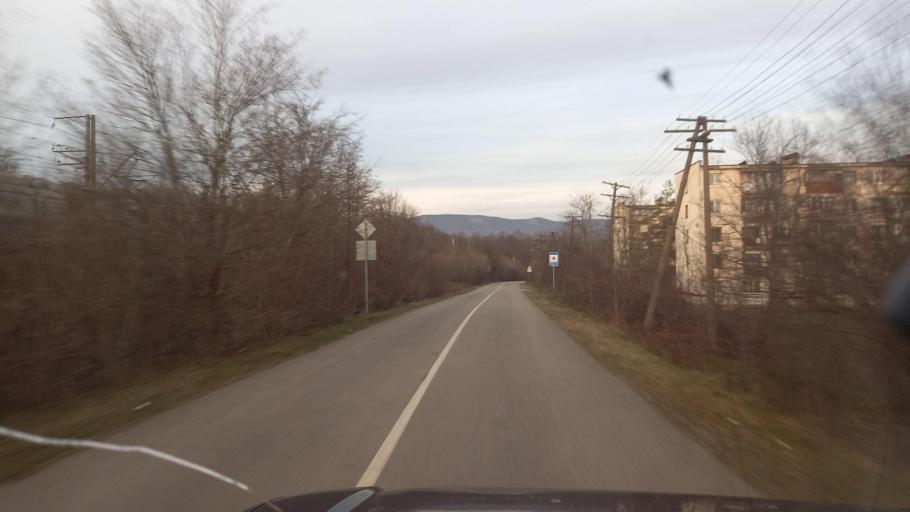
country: RU
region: Krasnodarskiy
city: Goryachiy Klyuch
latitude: 44.3886
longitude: 39.1924
